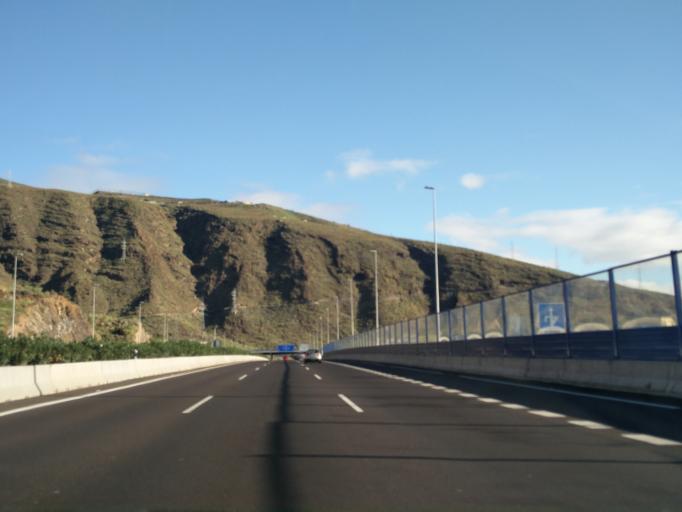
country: ES
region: Canary Islands
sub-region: Provincia de Santa Cruz de Tenerife
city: Candelaria
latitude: 28.3775
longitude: -16.3648
